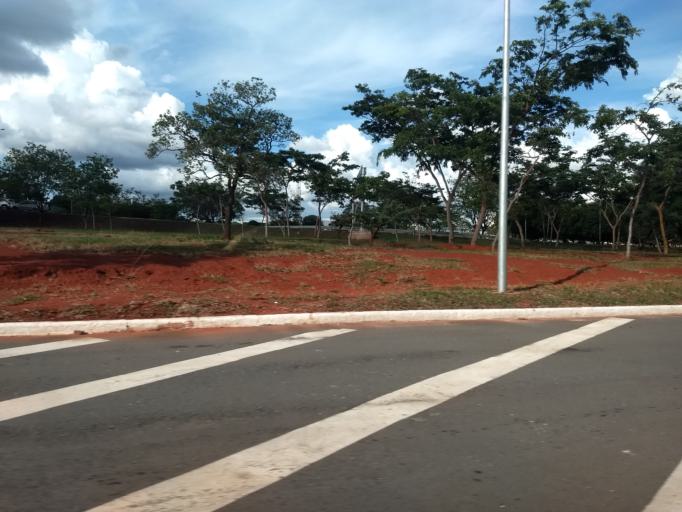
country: BR
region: Federal District
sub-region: Brasilia
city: Brasilia
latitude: -15.7761
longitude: -47.9360
